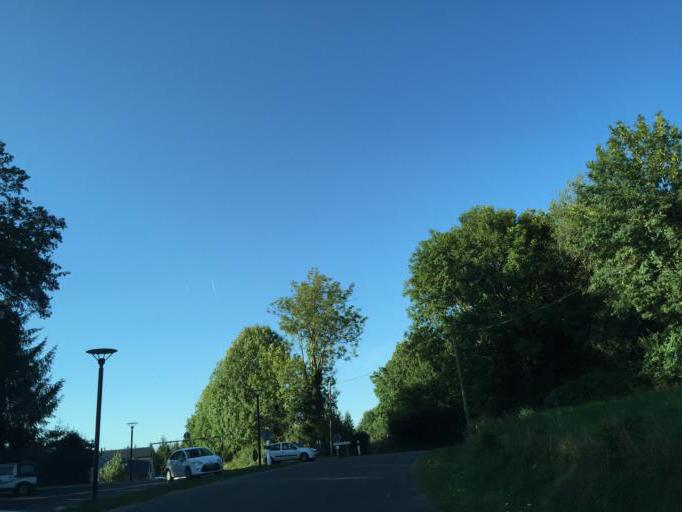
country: FR
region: Midi-Pyrenees
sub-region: Departement de l'Aveyron
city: Salles-Curan
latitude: 44.2070
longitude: 2.7775
